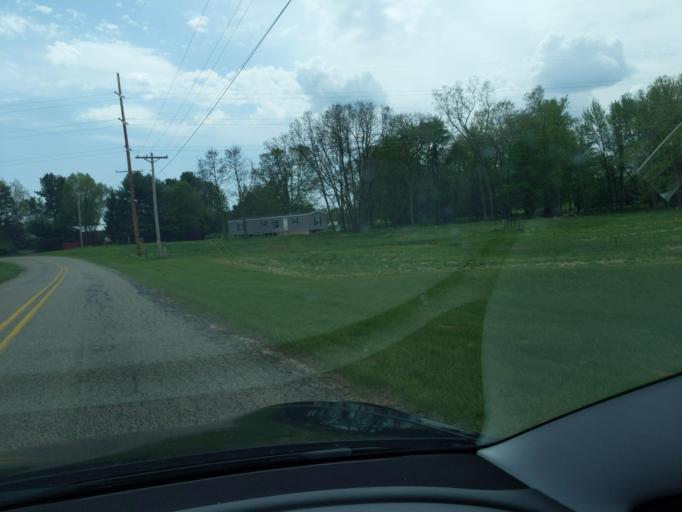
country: US
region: Michigan
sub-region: Ingham County
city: Leslie
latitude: 42.5010
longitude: -84.3402
